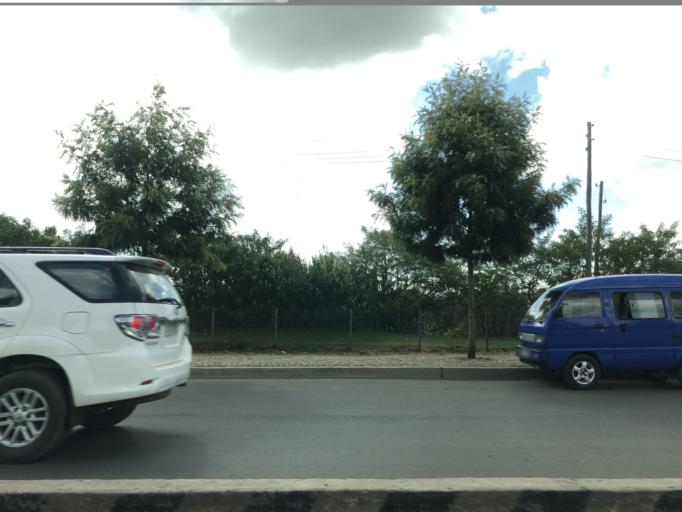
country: ET
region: Adis Abeba
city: Addis Ababa
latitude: 9.0206
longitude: 38.7822
